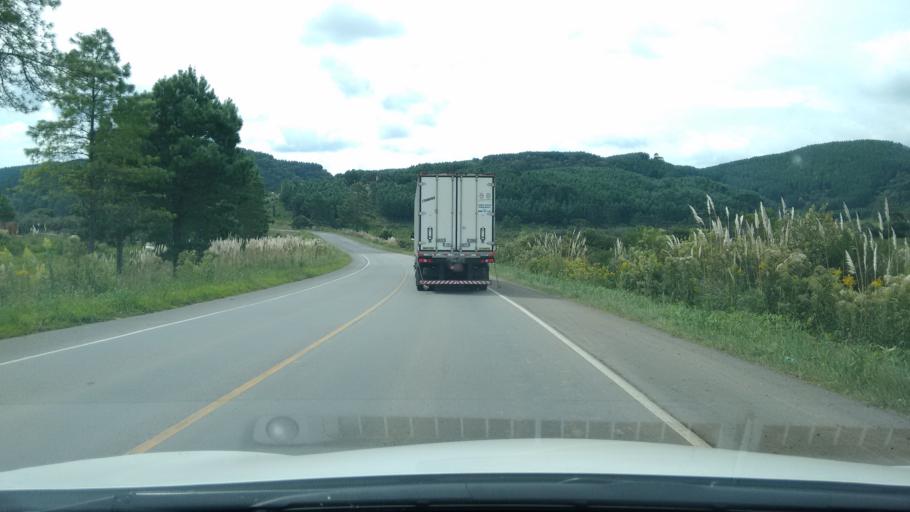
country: BR
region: Santa Catarina
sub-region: Otacilio Costa
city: Otacilio Costa
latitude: -27.3094
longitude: -50.2386
